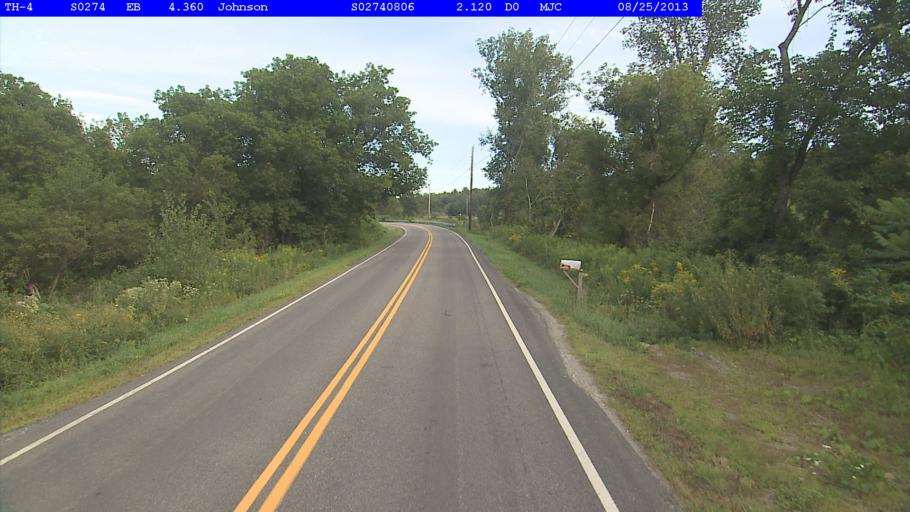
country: US
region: Vermont
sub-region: Lamoille County
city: Johnson
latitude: 44.6441
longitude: -72.7148
